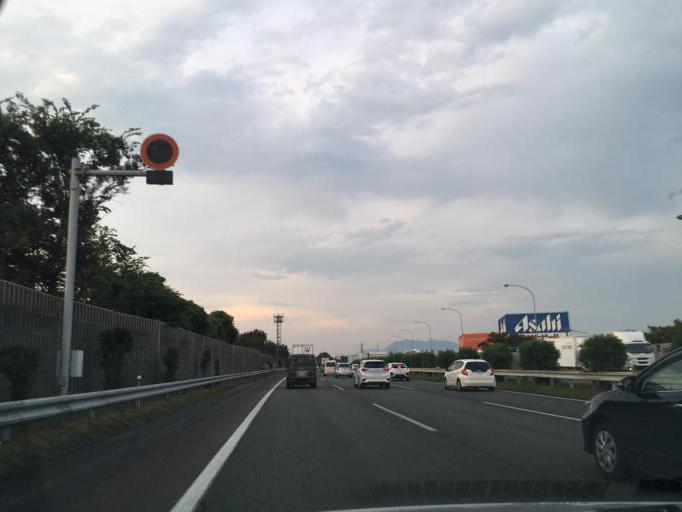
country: JP
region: Saga Prefecture
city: Tosu
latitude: 33.4059
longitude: 130.5378
